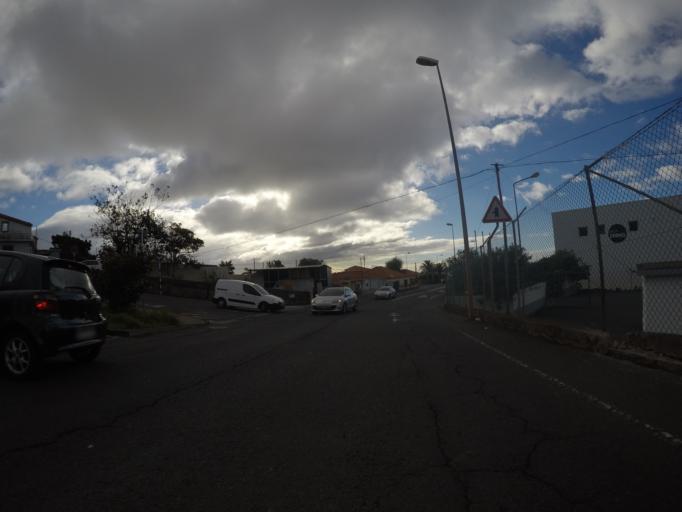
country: PT
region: Madeira
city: Canico
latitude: 32.6460
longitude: -16.8570
